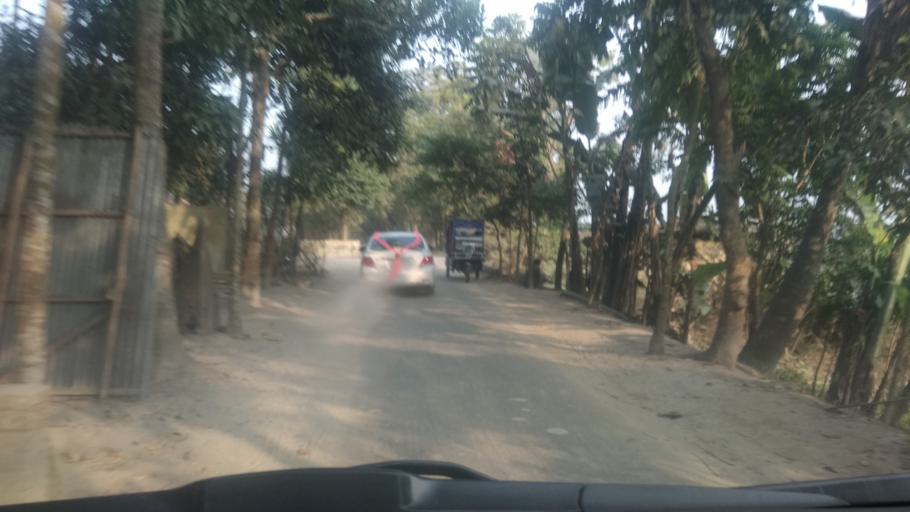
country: BD
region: Dhaka
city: Netrakona
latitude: 24.7758
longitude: 90.6033
